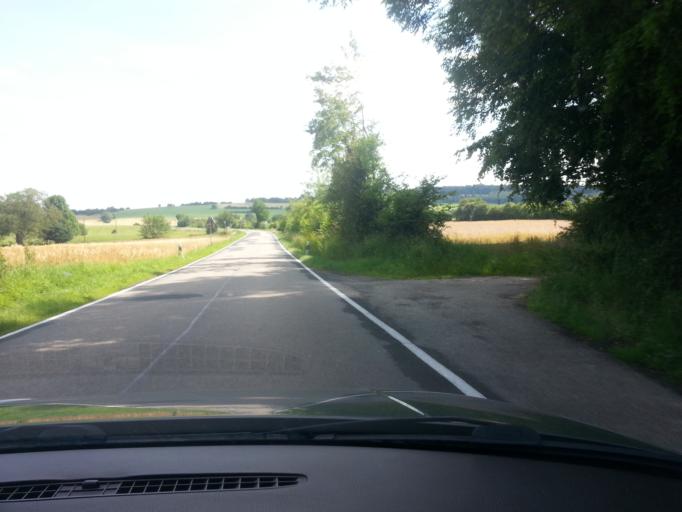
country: DE
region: Saarland
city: Blieskastel
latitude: 49.2038
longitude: 7.2803
